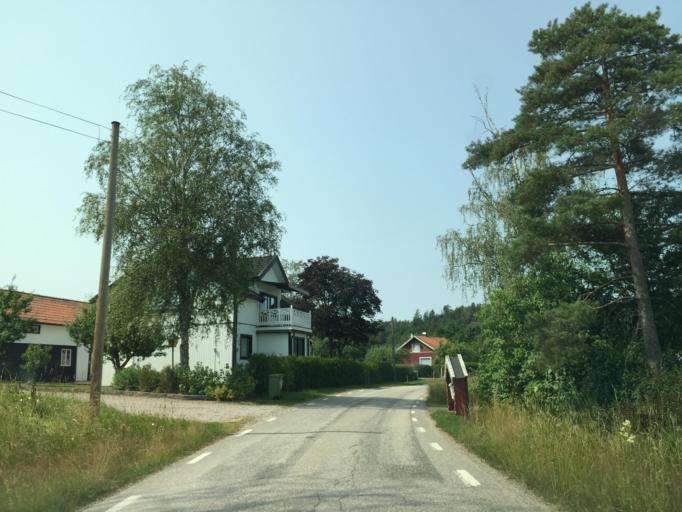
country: SE
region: Vaestra Goetaland
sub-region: Lilla Edets Kommun
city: Lilla Edet
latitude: 58.2119
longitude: 12.1364
